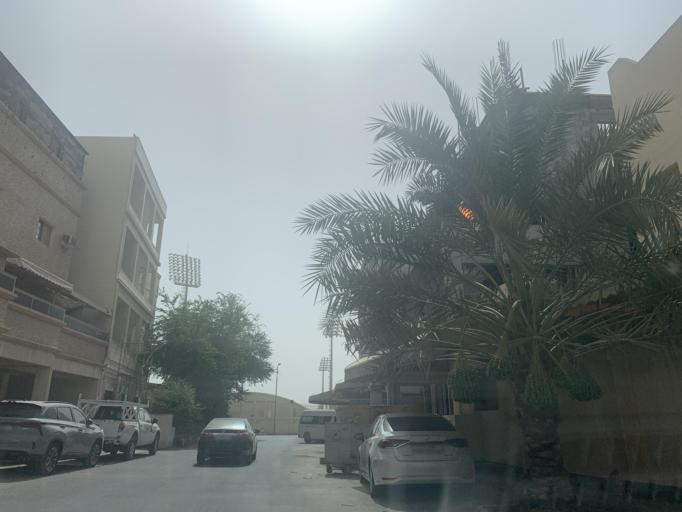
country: BH
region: Manama
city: Jidd Hafs
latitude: 26.2190
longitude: 50.5427
